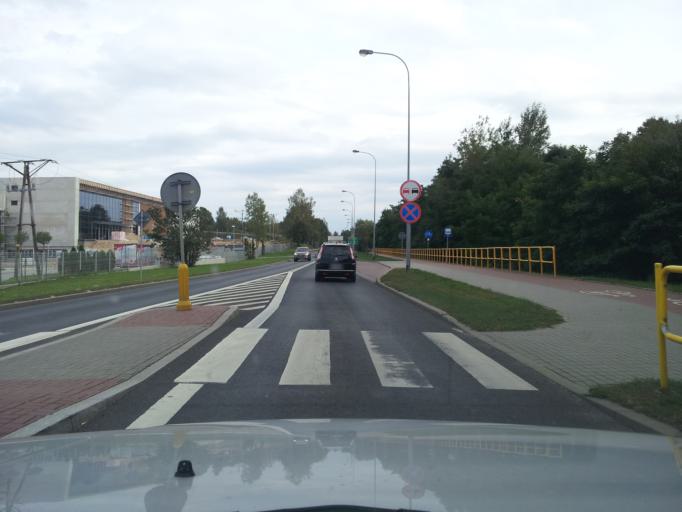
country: PL
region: Warmian-Masurian Voivodeship
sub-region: Powiat ostrodzki
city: Ostroda
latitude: 53.6847
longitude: 19.9918
